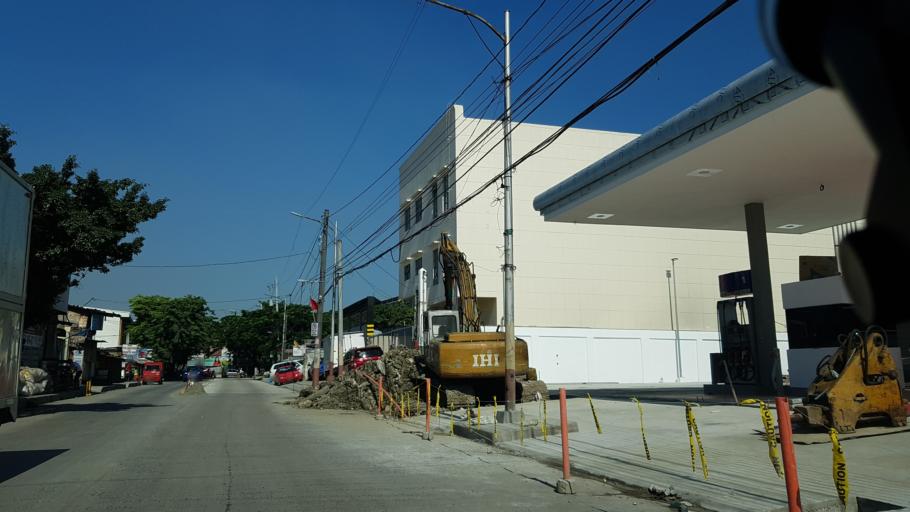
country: PH
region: Metro Manila
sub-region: Pasig
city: Pasig City
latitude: 14.5716
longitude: 121.0891
